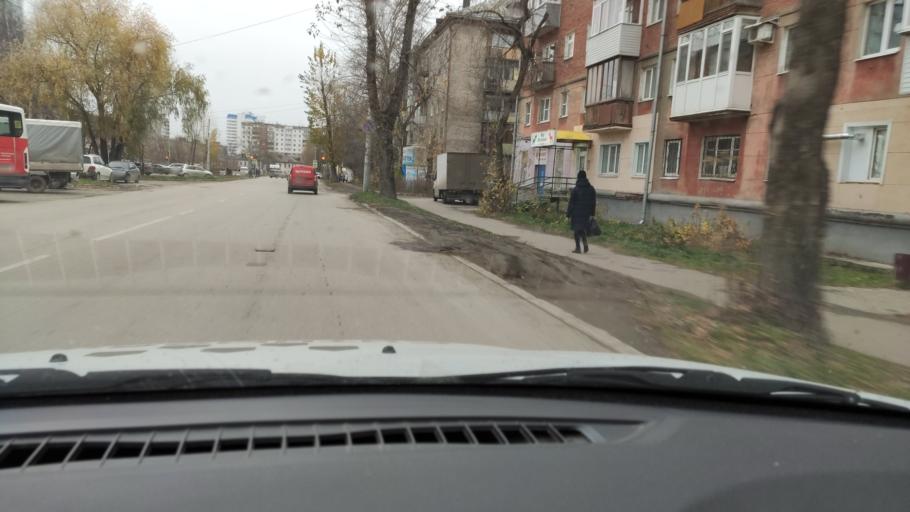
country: RU
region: Perm
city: Perm
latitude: 57.9654
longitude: 56.2248
